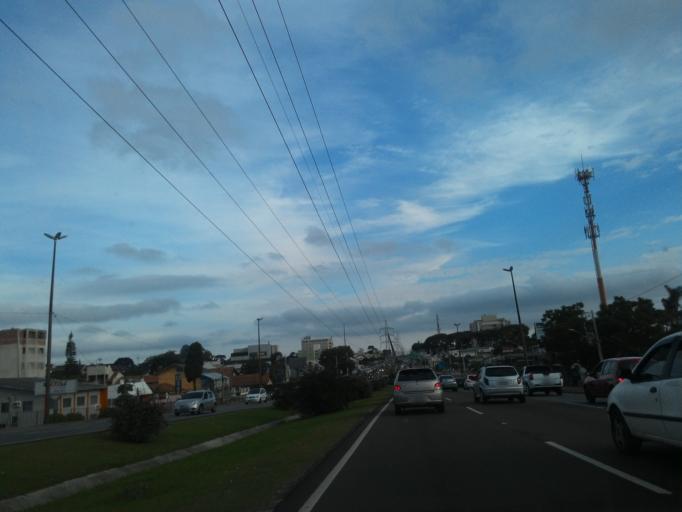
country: BR
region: Parana
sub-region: Curitiba
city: Curitiba
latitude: -25.4537
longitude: -49.2428
